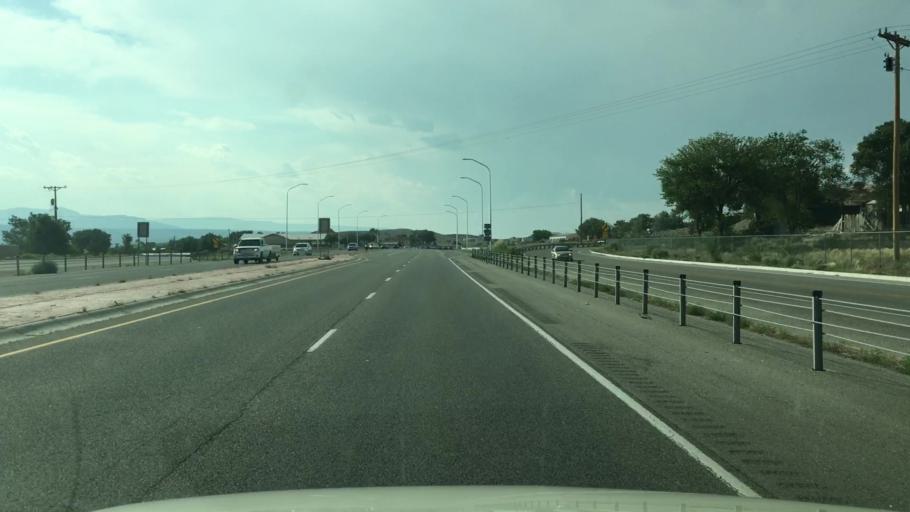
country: US
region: New Mexico
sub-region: Santa Fe County
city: El Valle de Arroyo Seco
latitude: 35.9677
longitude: -106.0359
